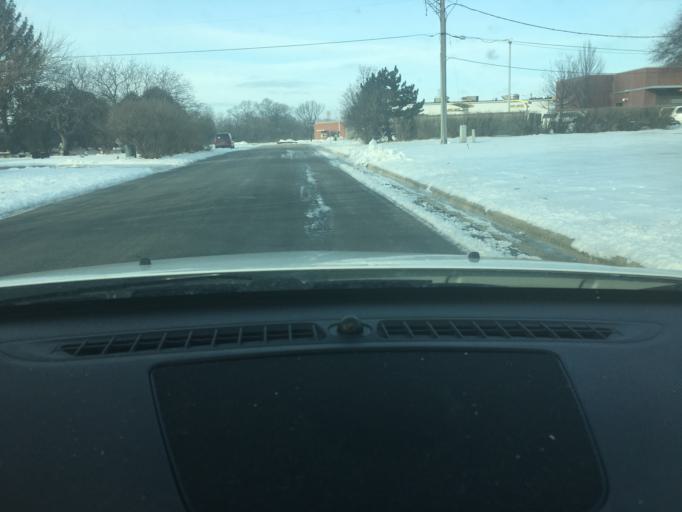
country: US
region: Illinois
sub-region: LaSalle County
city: Peru
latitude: 41.3378
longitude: -89.1169
